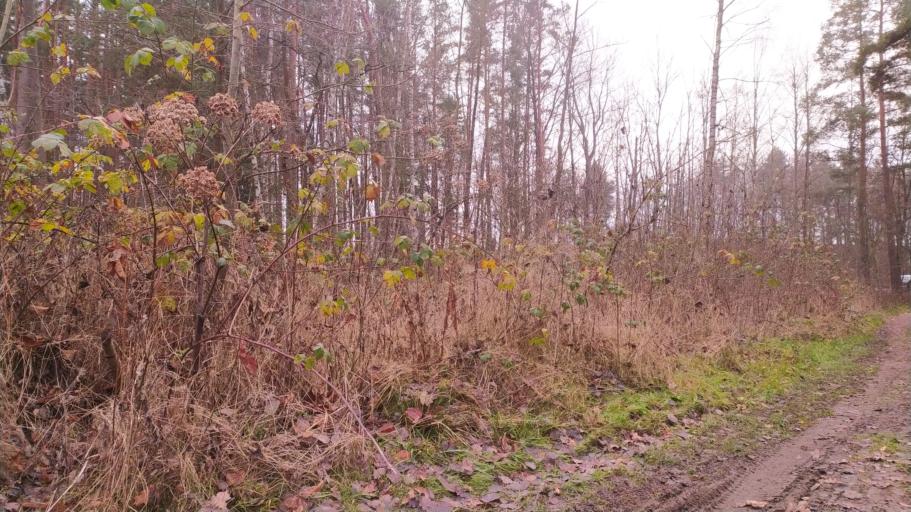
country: DE
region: Bavaria
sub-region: Upper Franconia
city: Schirnding
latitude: 50.0999
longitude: 12.2762
